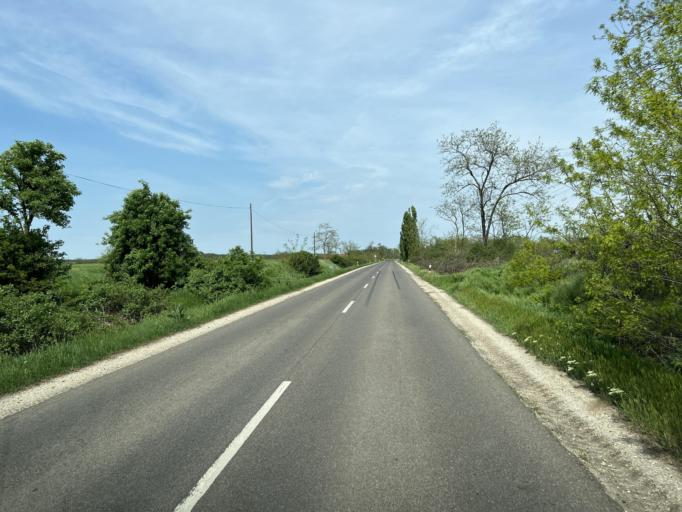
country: HU
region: Pest
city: Abony
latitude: 47.2198
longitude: 19.9760
